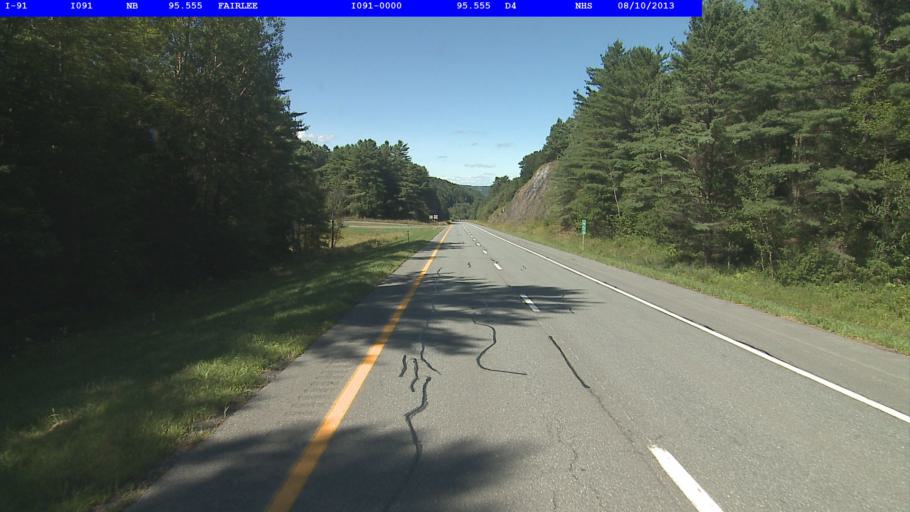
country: US
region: New Hampshire
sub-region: Grafton County
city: Orford
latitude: 43.9553
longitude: -72.1294
